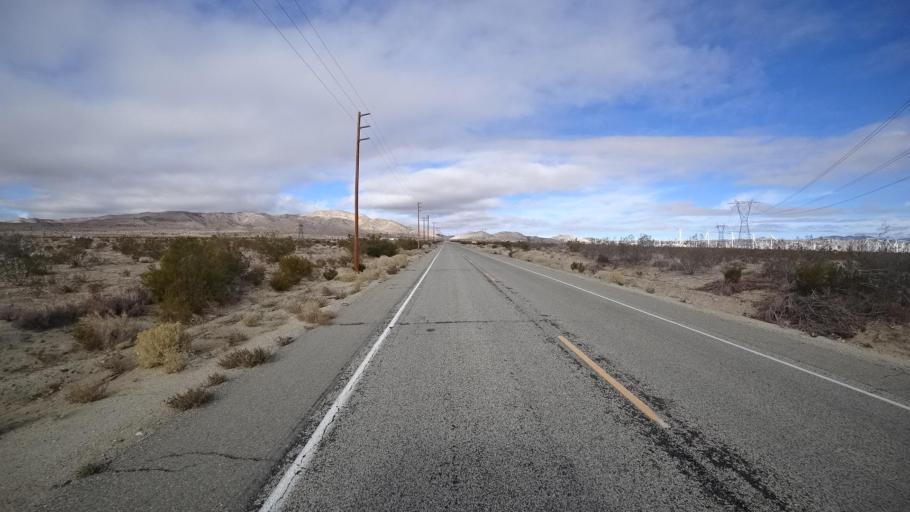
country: US
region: California
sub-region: Kern County
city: Mojave
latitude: 34.9823
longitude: -118.3157
